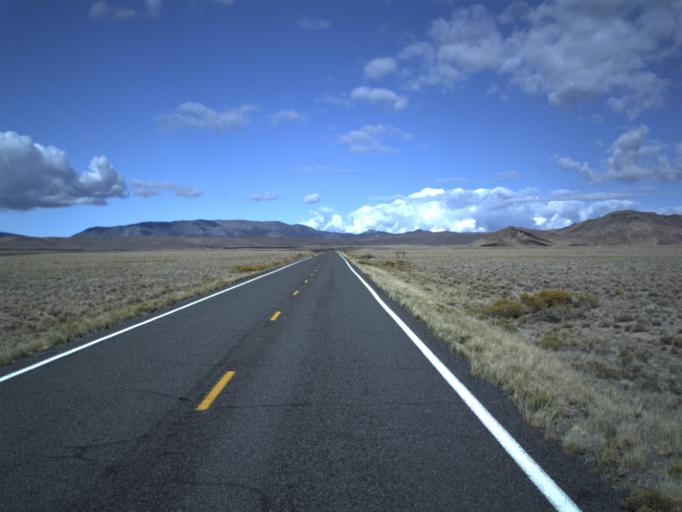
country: US
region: Utah
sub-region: Beaver County
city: Milford
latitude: 38.5640
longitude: -113.7677
